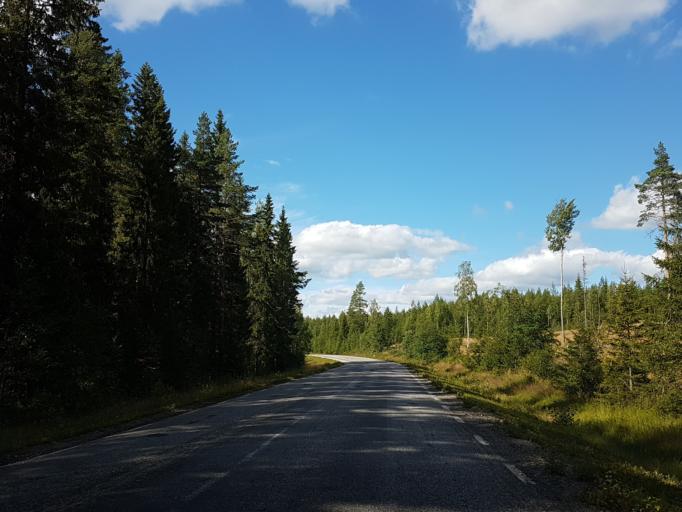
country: SE
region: Vaesterbotten
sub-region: Umea Kommun
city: Saevar
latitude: 64.2193
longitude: 20.4755
